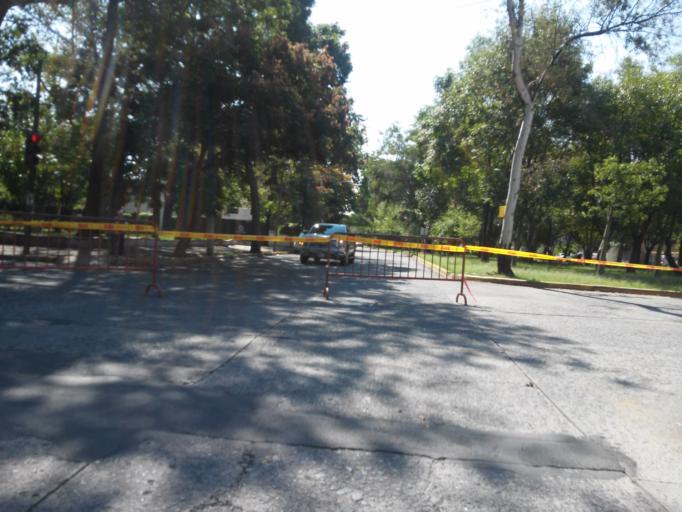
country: MX
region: Jalisco
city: Guadalajara
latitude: 20.6632
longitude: -103.3855
